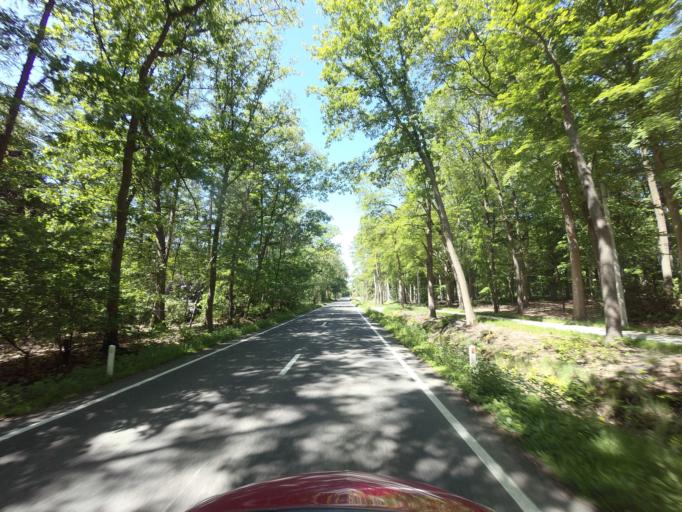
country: BE
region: Flanders
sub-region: Provincie Antwerpen
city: Arendonk
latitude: 51.3528
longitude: 5.0622
